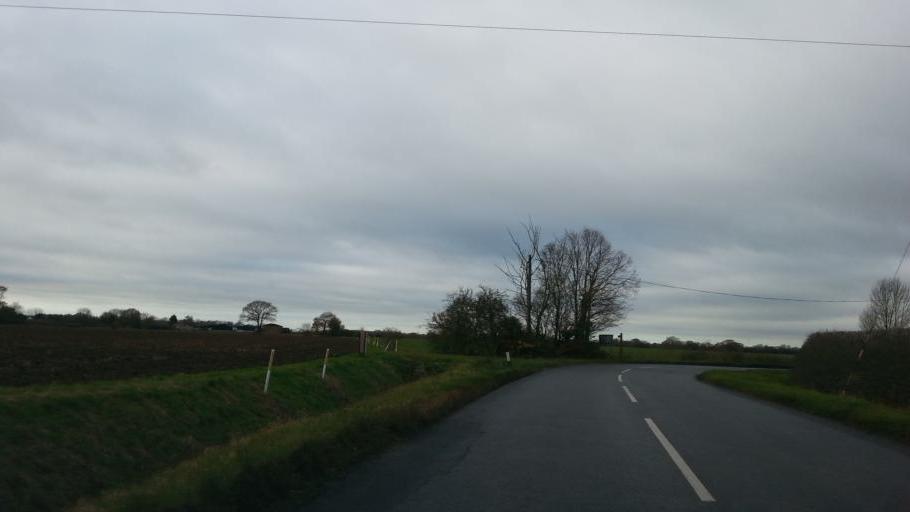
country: GB
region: England
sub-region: Suffolk
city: Framlingham
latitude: 52.2970
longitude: 1.3374
